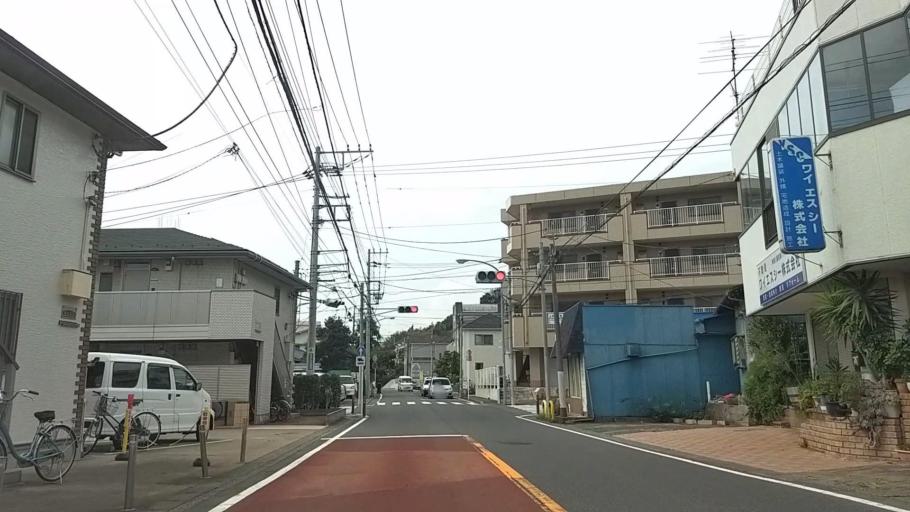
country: JP
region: Kanagawa
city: Yokohama
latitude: 35.5176
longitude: 139.5589
